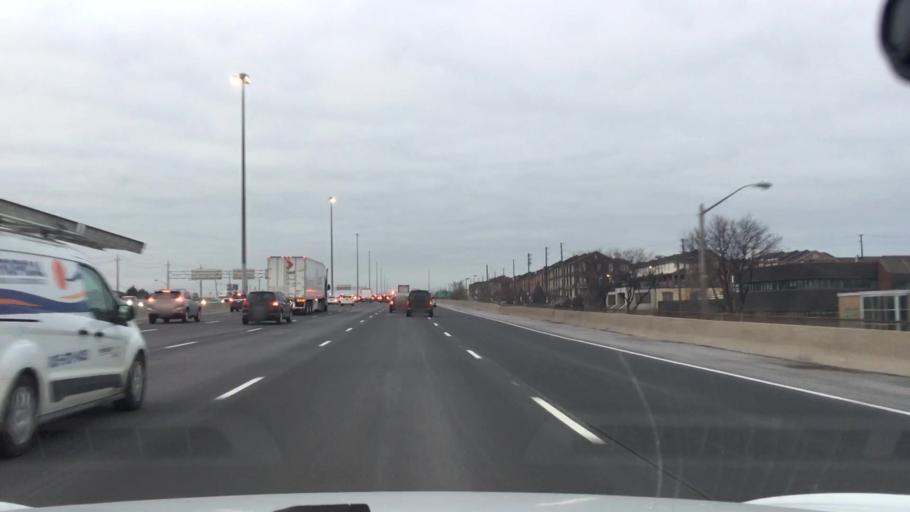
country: CA
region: Ontario
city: Etobicoke
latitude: 43.7237
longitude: -79.5230
